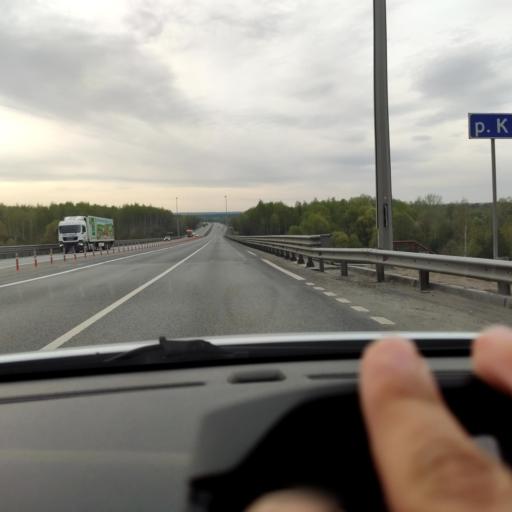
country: RU
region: Tatarstan
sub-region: Gorod Kazan'
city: Kazan
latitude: 55.9134
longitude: 49.1603
